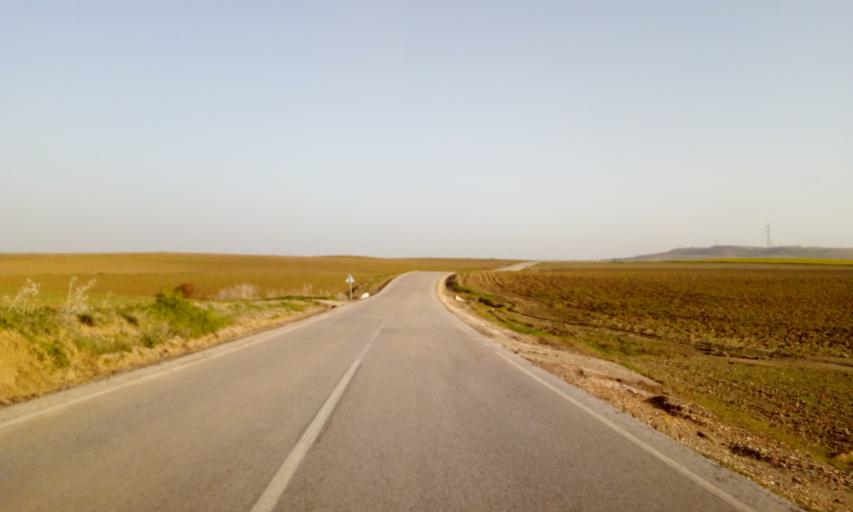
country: ES
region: Andalusia
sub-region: Provincia de Sevilla
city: Salteras
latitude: 37.4482
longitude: -6.1109
